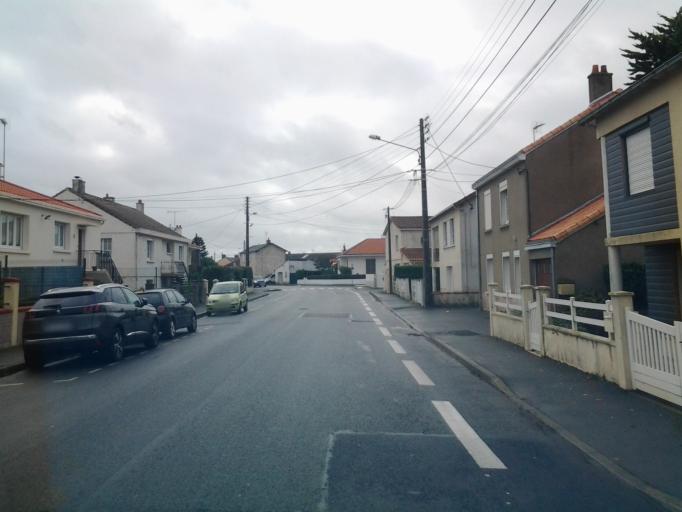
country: FR
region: Pays de la Loire
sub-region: Departement de la Vendee
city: La Roche-sur-Yon
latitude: 46.6634
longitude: -1.4001
